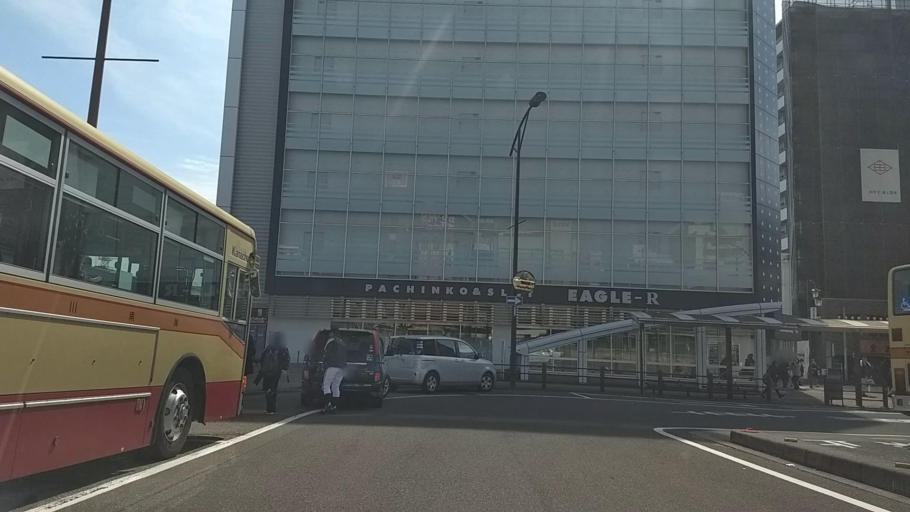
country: JP
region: Kanagawa
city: Fujisawa
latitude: 35.3963
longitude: 139.4662
